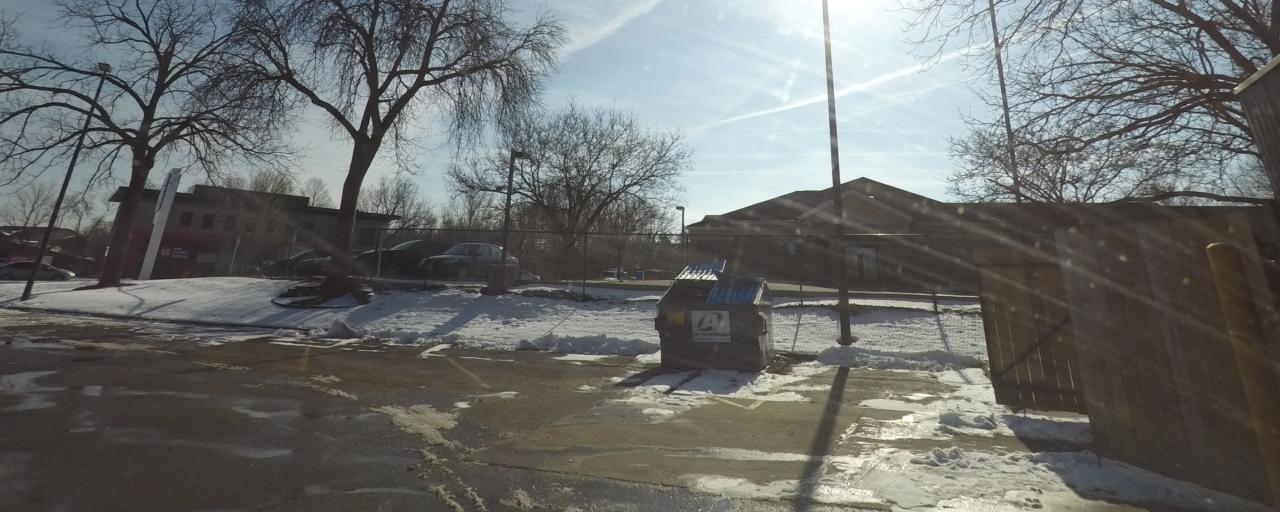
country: US
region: Wisconsin
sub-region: Dane County
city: Madison
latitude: 43.0294
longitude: -89.4115
